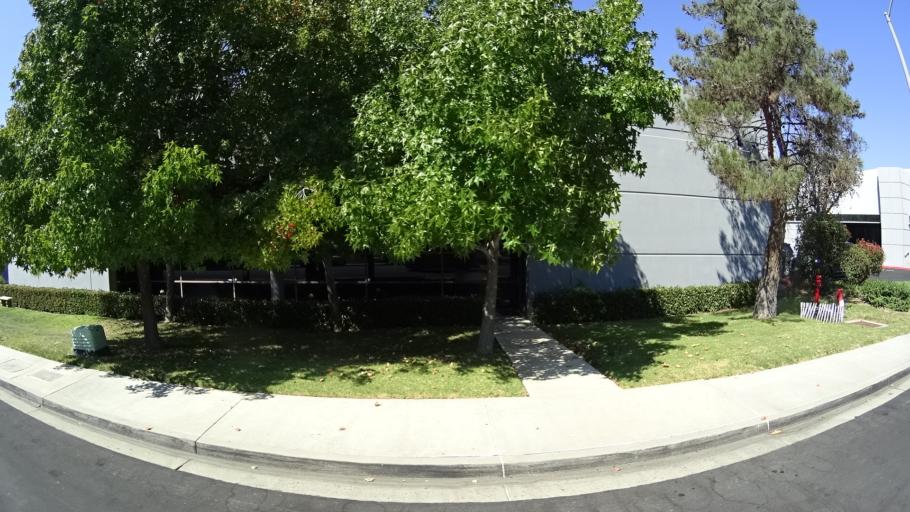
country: US
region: California
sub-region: Orange County
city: San Clemente
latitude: 33.4546
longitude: -117.6010
